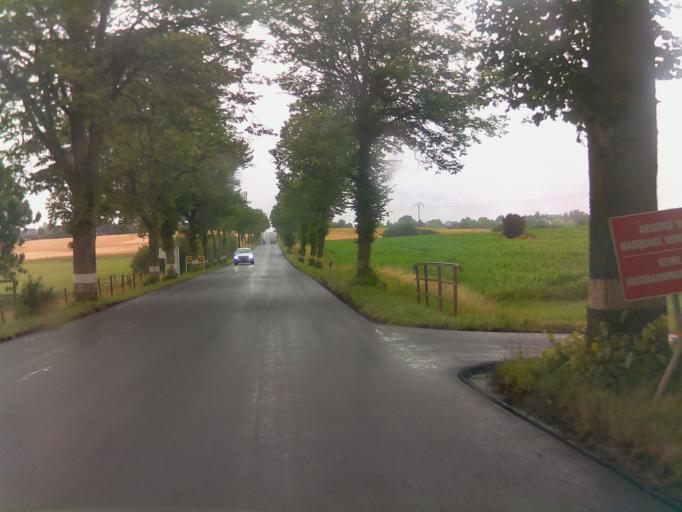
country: LU
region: Luxembourg
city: Bergem
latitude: 49.5180
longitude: 6.0579
